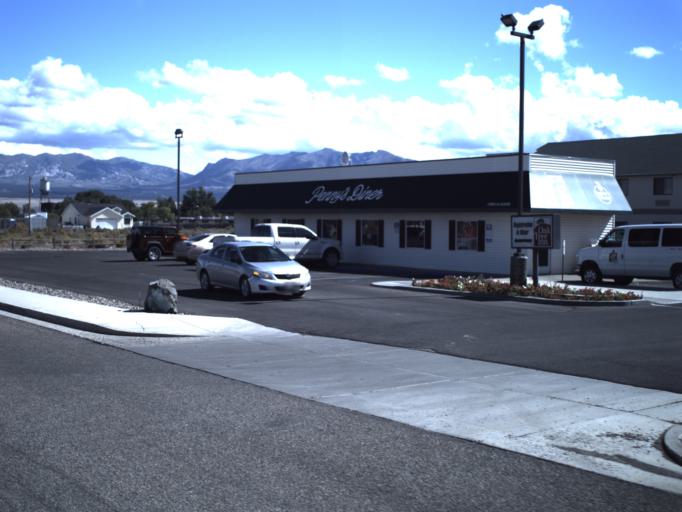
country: US
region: Utah
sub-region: Beaver County
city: Milford
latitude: 38.3970
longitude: -113.0209
